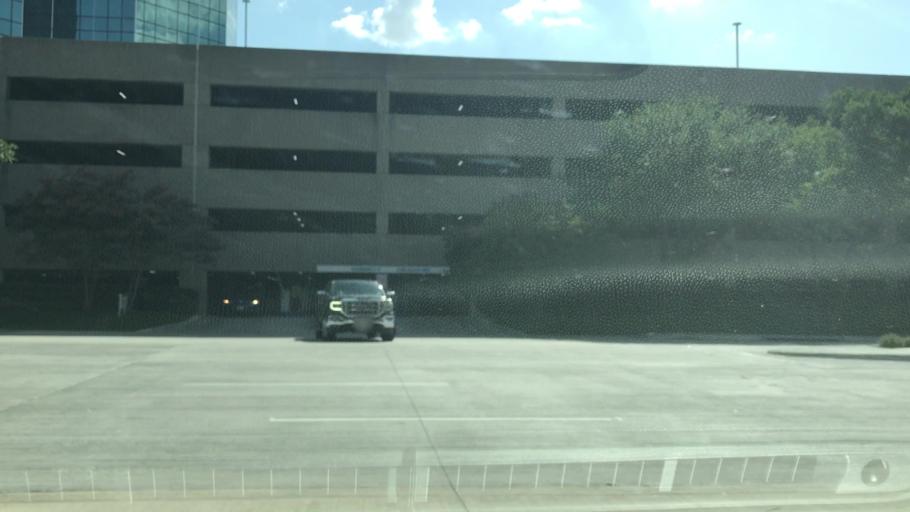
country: US
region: Texas
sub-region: Dallas County
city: Irving
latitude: 32.8722
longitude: -96.9429
